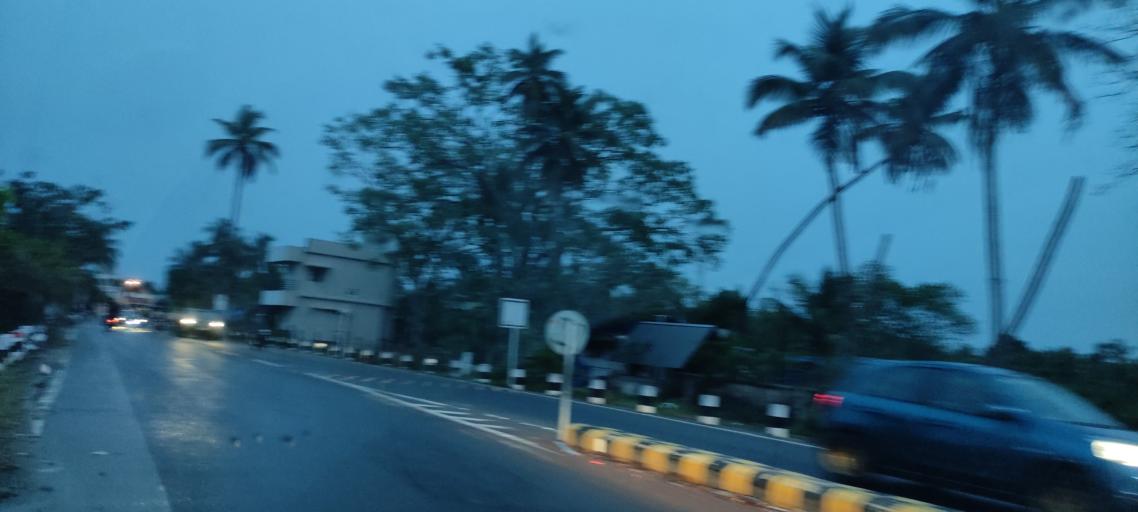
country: IN
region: Kerala
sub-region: Ernakulam
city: Cochin
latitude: 9.9206
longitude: 76.2873
